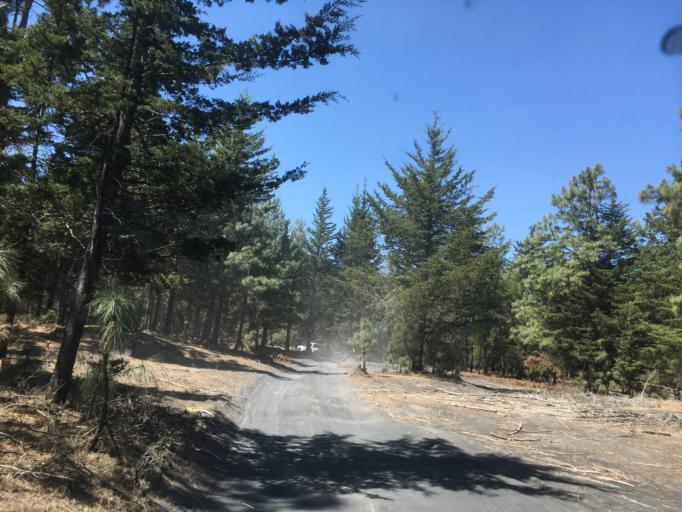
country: MX
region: Michoacan
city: Angahuan
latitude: 19.4634
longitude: -102.2335
